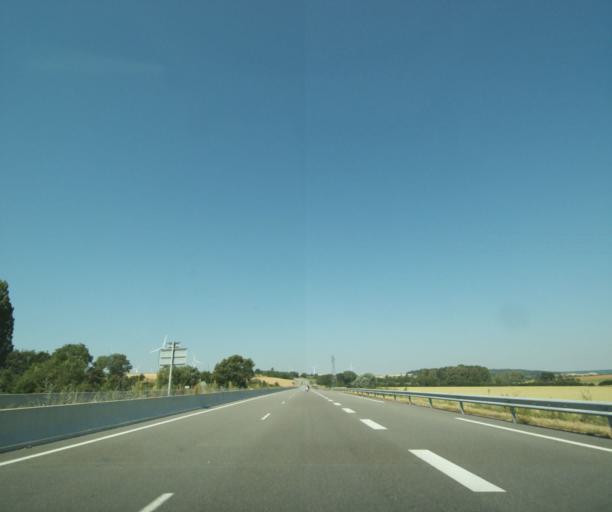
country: FR
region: Lorraine
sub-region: Departement de la Meuse
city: Lerouville
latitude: 48.7049
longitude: 5.4615
